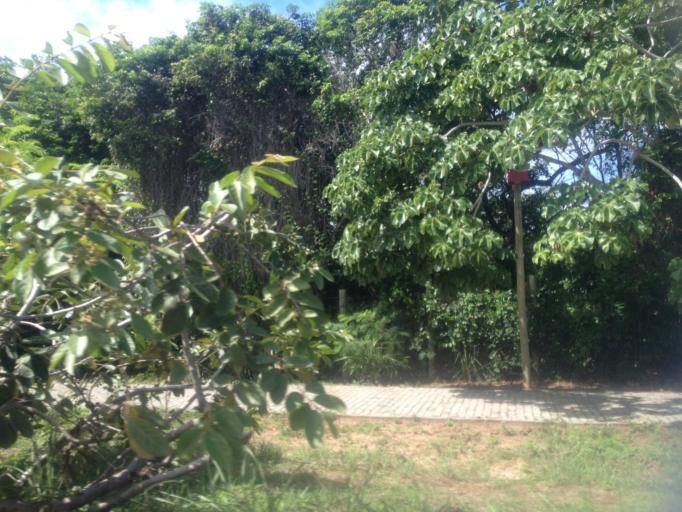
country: BR
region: Bahia
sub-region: Mata De Sao Joao
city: Mata de Sao Joao
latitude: -12.5732
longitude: -38.0142
